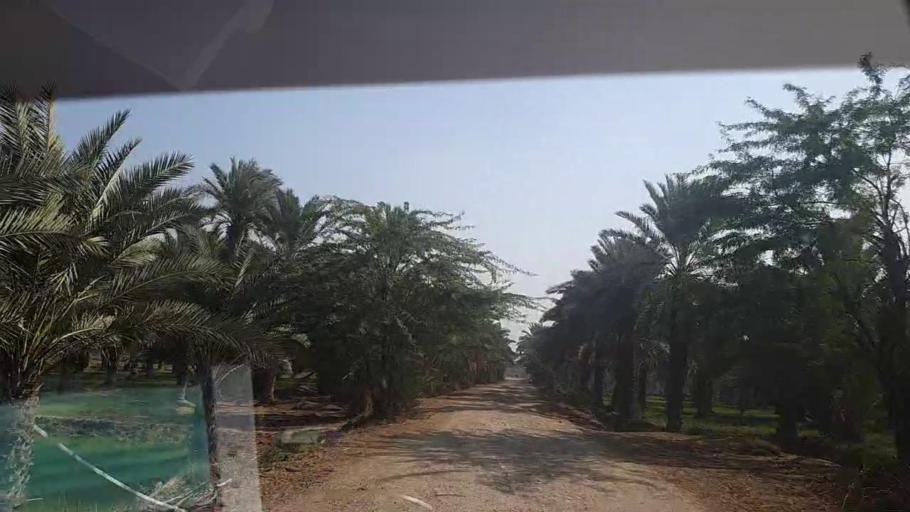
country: PK
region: Sindh
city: Kot Diji
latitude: 27.4343
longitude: 68.6861
